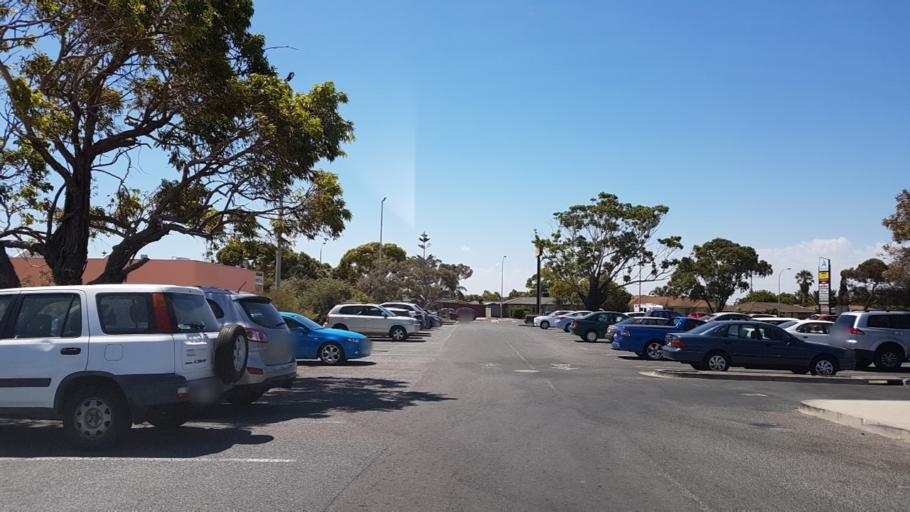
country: AU
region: South Australia
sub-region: Port Adelaide Enfield
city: Birkenhead
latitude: -34.7933
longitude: 138.4975
